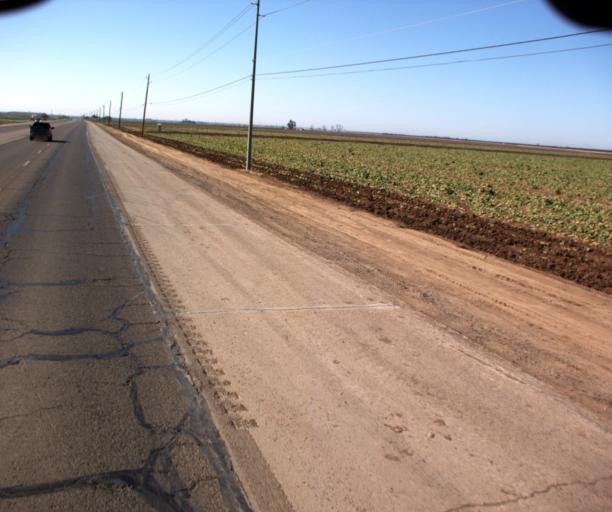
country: US
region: Arizona
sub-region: Yuma County
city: San Luis
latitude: 32.5415
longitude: -114.7869
